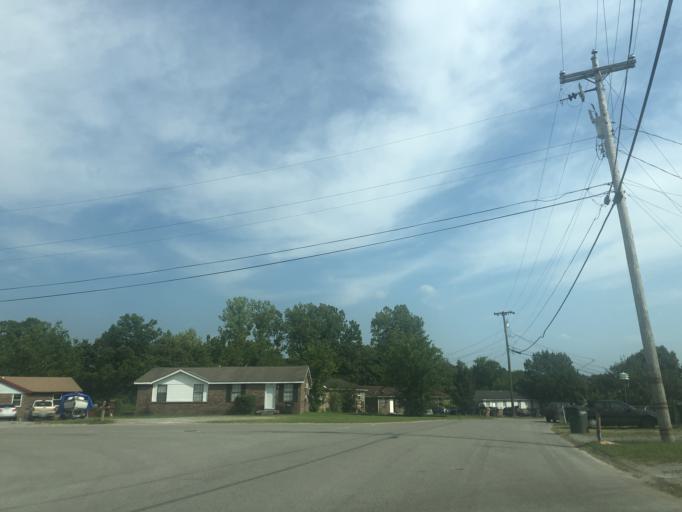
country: US
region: Tennessee
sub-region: Wilson County
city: Green Hill
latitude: 36.1778
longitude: -86.5862
